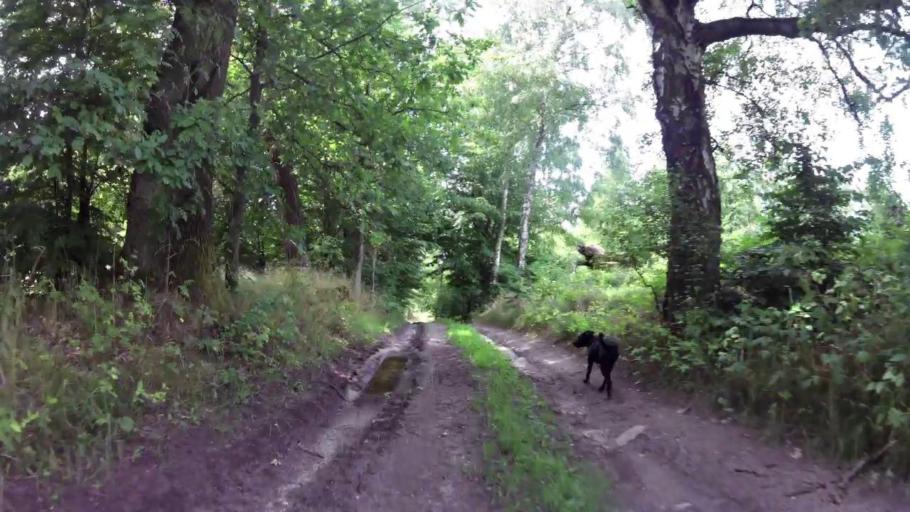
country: PL
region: West Pomeranian Voivodeship
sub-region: Powiat lobeski
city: Wegorzyno
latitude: 53.5139
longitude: 15.6732
